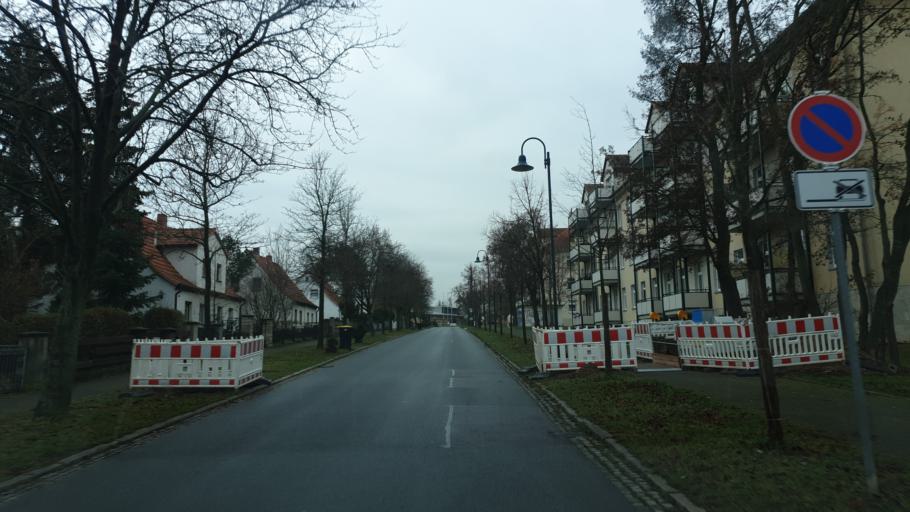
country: DE
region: Saxony-Anhalt
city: Naumburg
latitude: 51.1417
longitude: 11.7813
